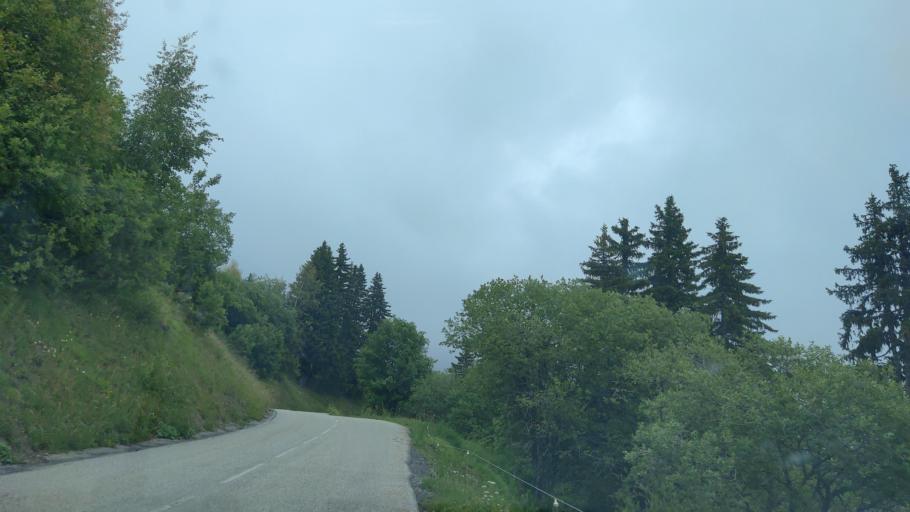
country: FR
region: Rhone-Alpes
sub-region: Departement de la Savoie
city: Beaufort
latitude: 45.7420
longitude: 6.5142
